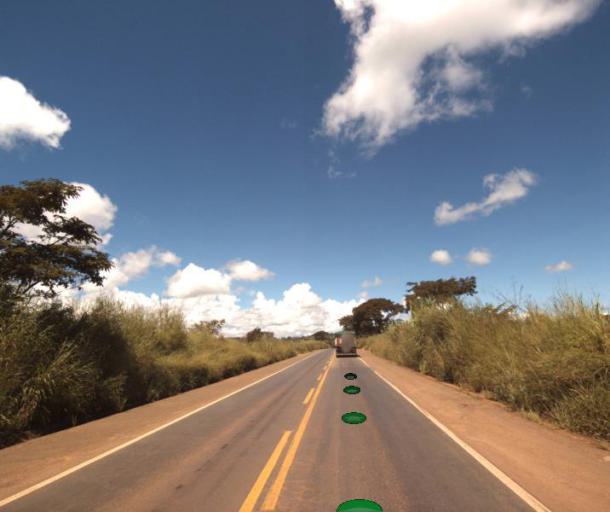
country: BR
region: Goias
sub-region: Anapolis
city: Anapolis
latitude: -16.1578
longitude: -49.0436
